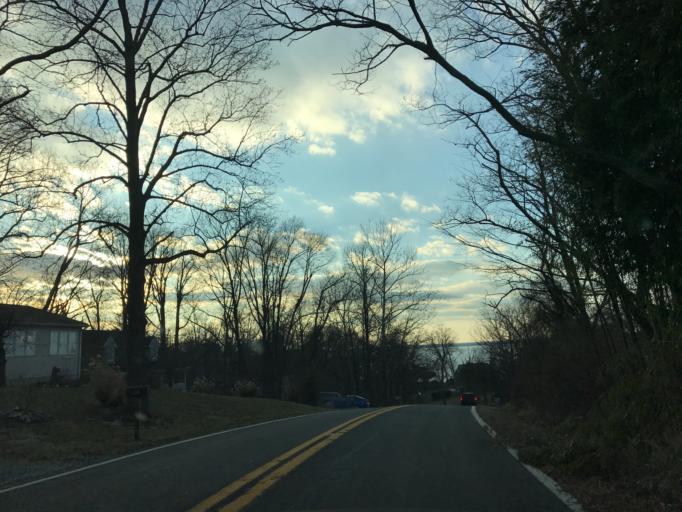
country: US
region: Maryland
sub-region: Cecil County
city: Charlestown
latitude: 39.4622
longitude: -75.9999
